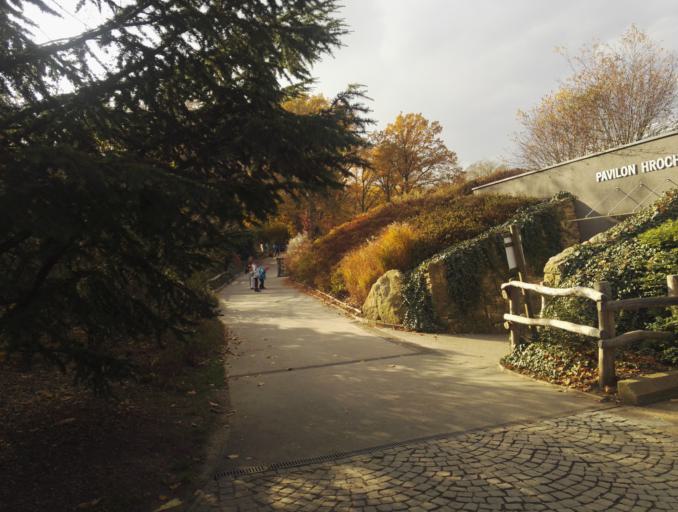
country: CZ
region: Praha
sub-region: Praha 1
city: Mala Strana
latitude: 50.1186
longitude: 14.4089
